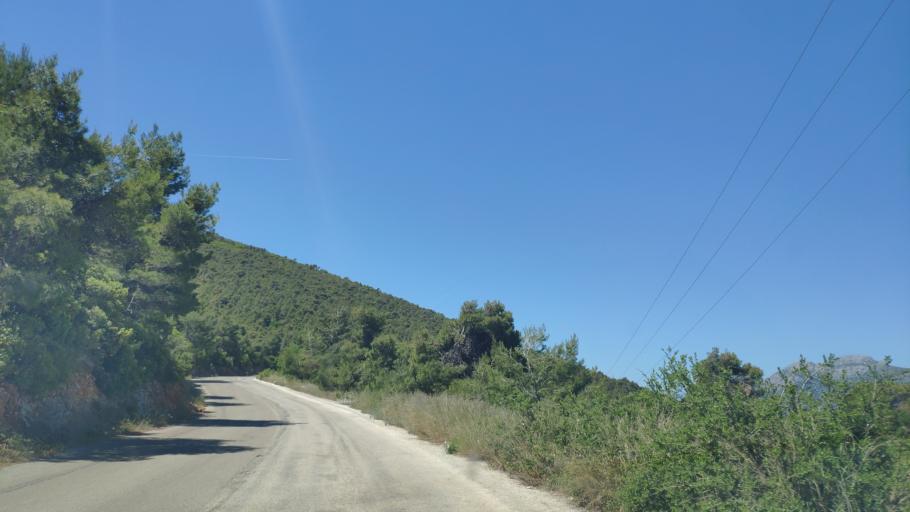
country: GR
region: Central Greece
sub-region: Nomos Voiotias
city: Kaparellion
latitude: 38.2031
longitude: 23.1603
